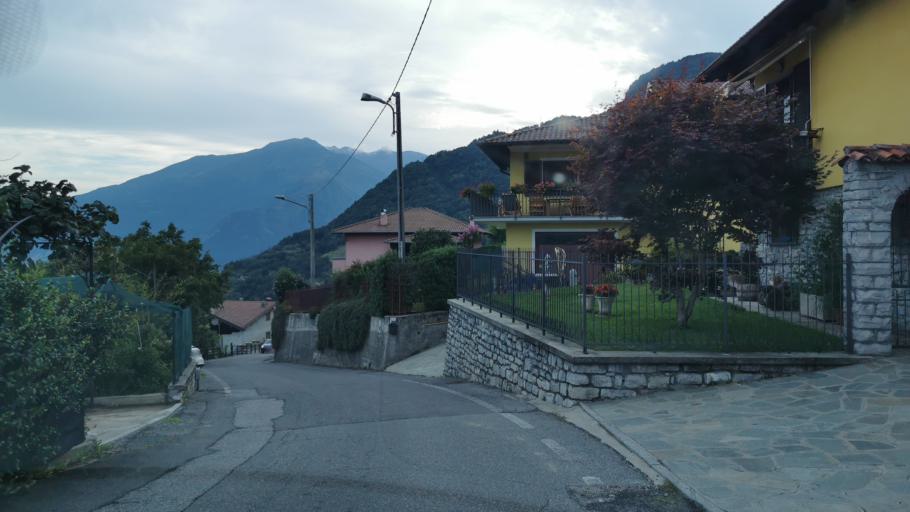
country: IT
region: Lombardy
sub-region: Provincia di Como
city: Vercana
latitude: 46.1614
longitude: 9.3337
